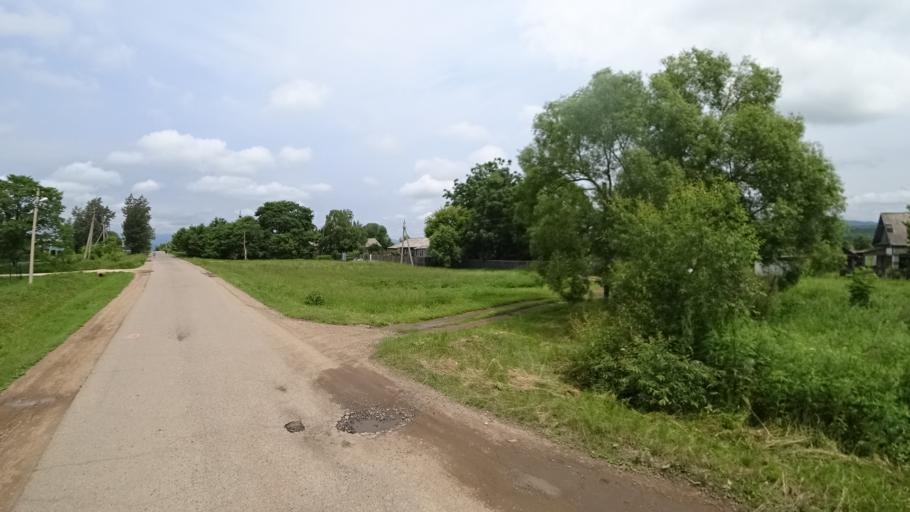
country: RU
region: Primorskiy
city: Novosysoyevka
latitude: 44.2301
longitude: 133.3608
